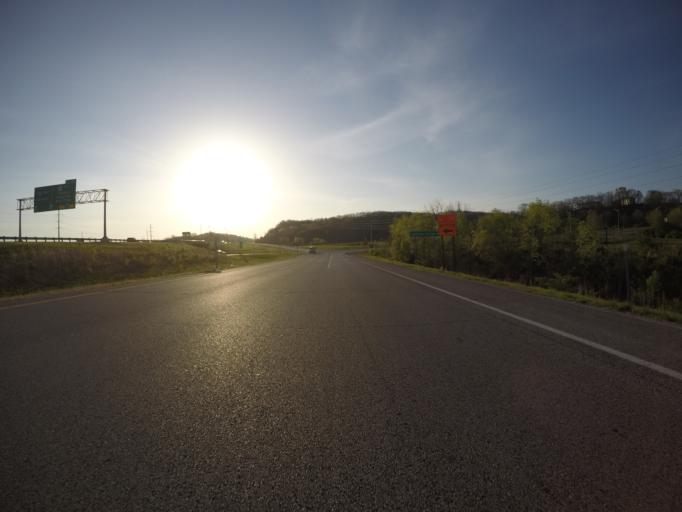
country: US
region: Missouri
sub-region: Jackson County
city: Lees Summit
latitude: 38.9361
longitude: -94.4492
